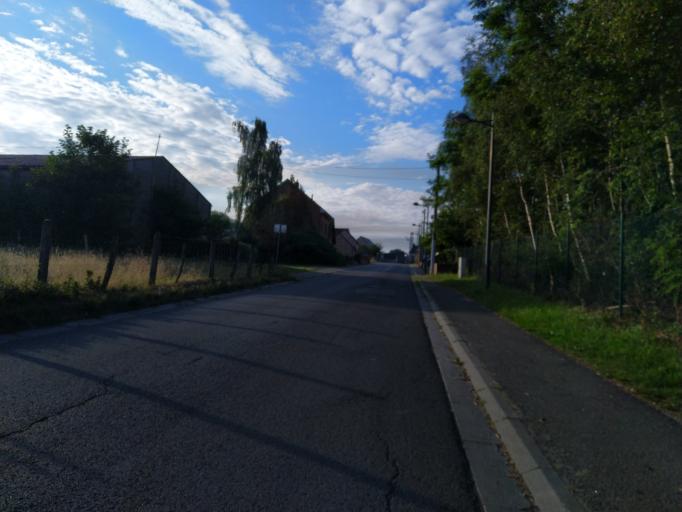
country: BE
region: Wallonia
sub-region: Province du Hainaut
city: Mons
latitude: 50.4824
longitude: 4.0285
